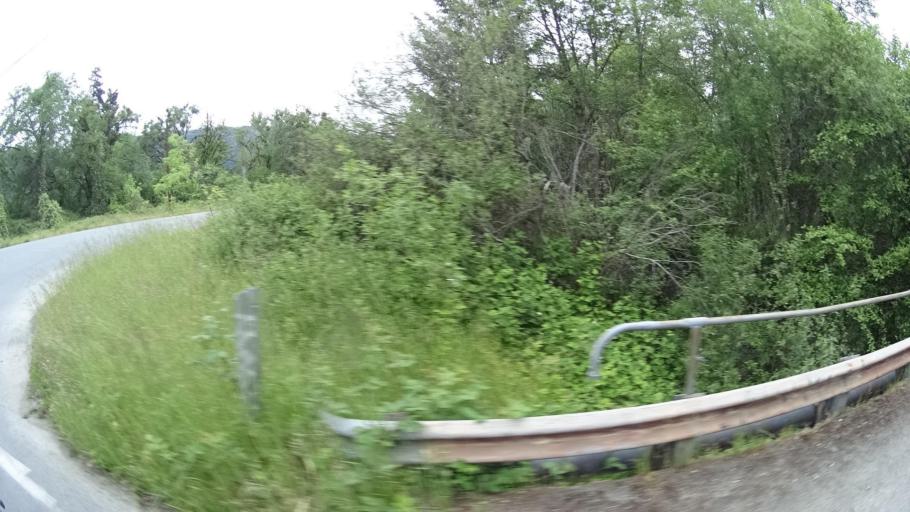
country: US
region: California
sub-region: Humboldt County
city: Willow Creek
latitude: 41.0868
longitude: -123.7090
